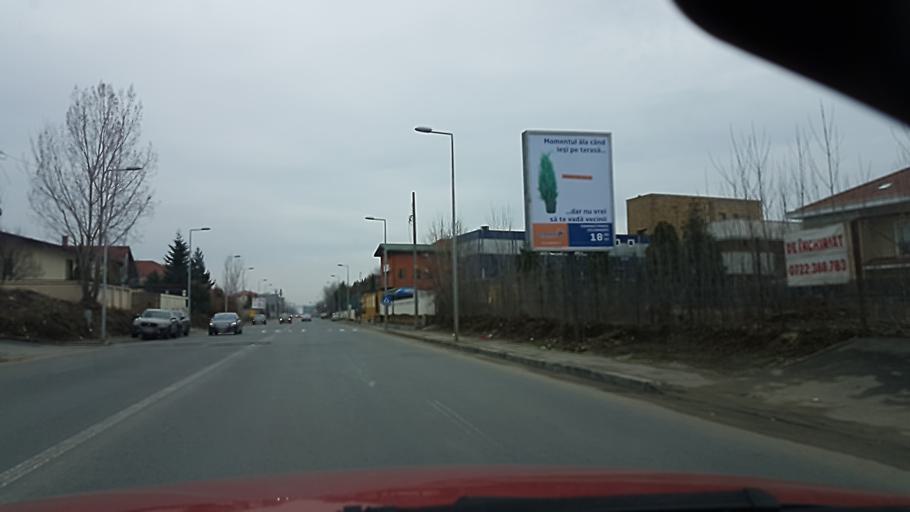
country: RO
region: Ilfov
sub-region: Comuna Tunari
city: Tunari
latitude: 44.5161
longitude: 26.1414
